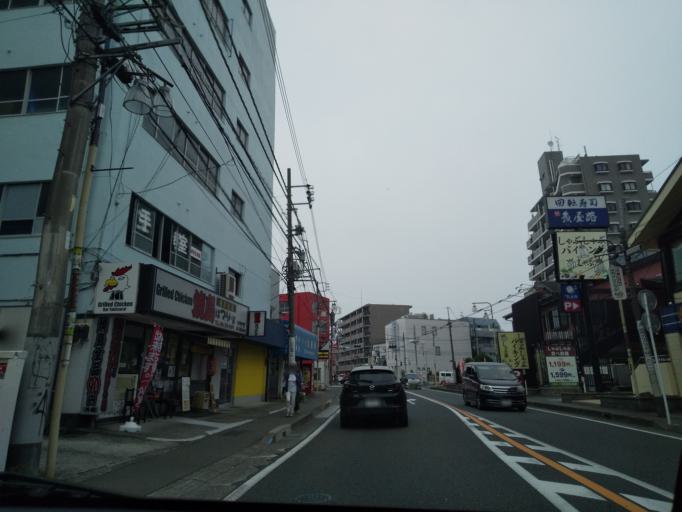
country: JP
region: Kanagawa
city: Zama
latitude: 35.5005
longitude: 139.4089
